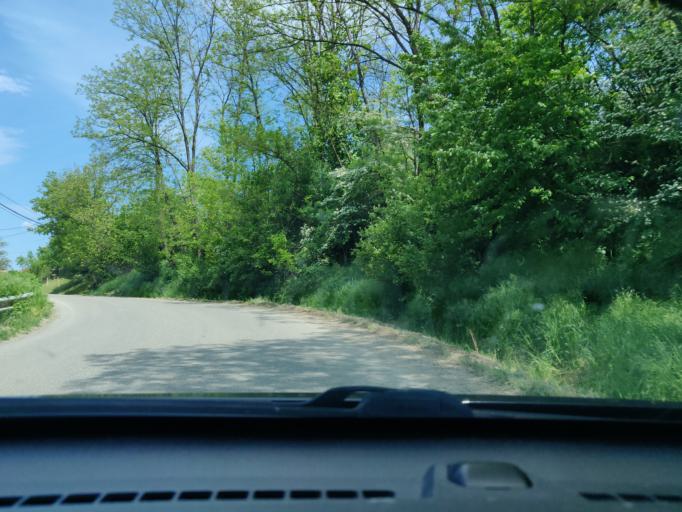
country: RO
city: Vizantea-Manastireasca
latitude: 45.9564
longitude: 26.8302
